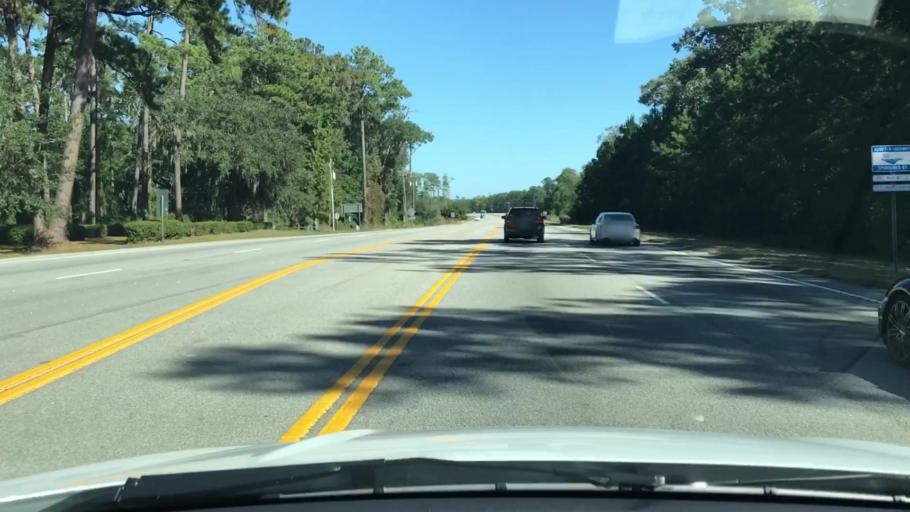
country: US
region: South Carolina
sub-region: Beaufort County
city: Laurel Bay
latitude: 32.3641
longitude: -80.8673
